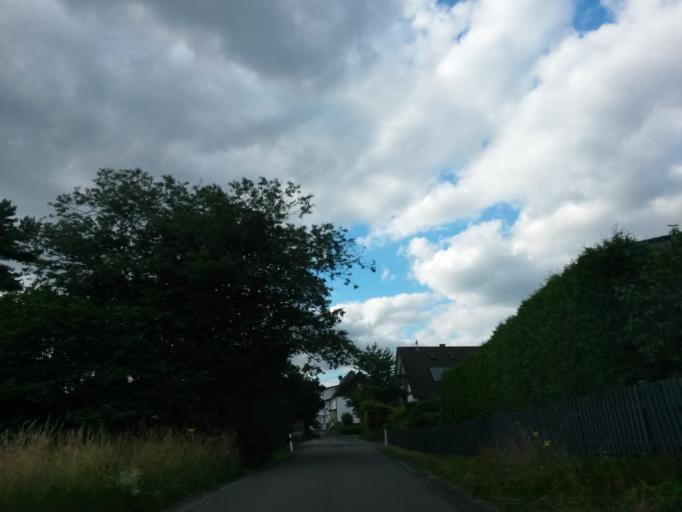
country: DE
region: North Rhine-Westphalia
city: Waldbrol
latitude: 50.9171
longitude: 7.6285
